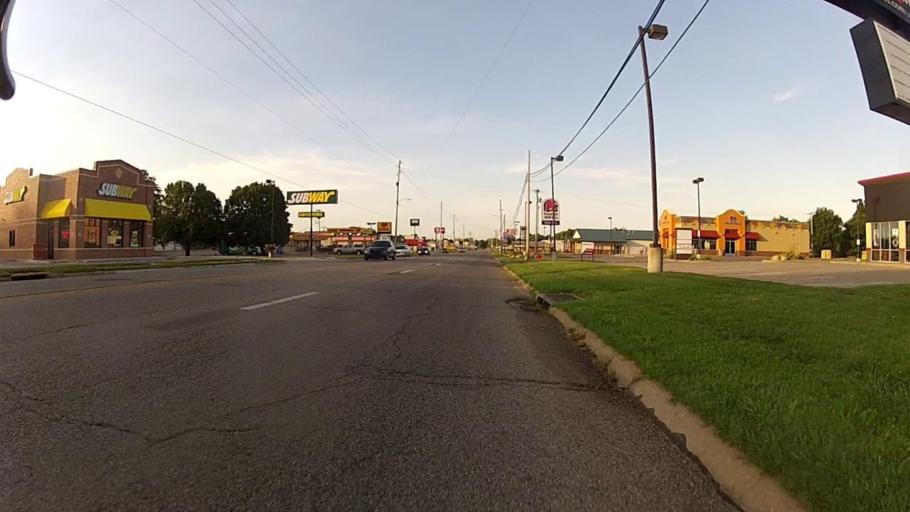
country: US
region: Kansas
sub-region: Cowley County
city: Arkansas City
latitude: 37.0838
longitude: -97.0402
